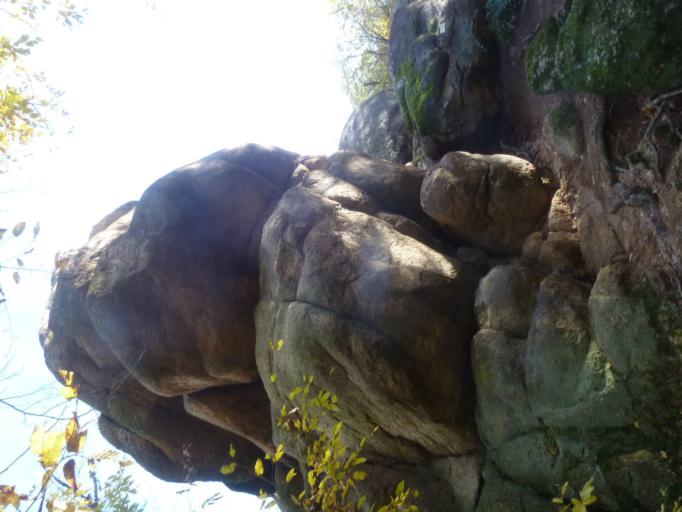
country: HU
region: Fejer
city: Pakozd
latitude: 47.2382
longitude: 18.5404
